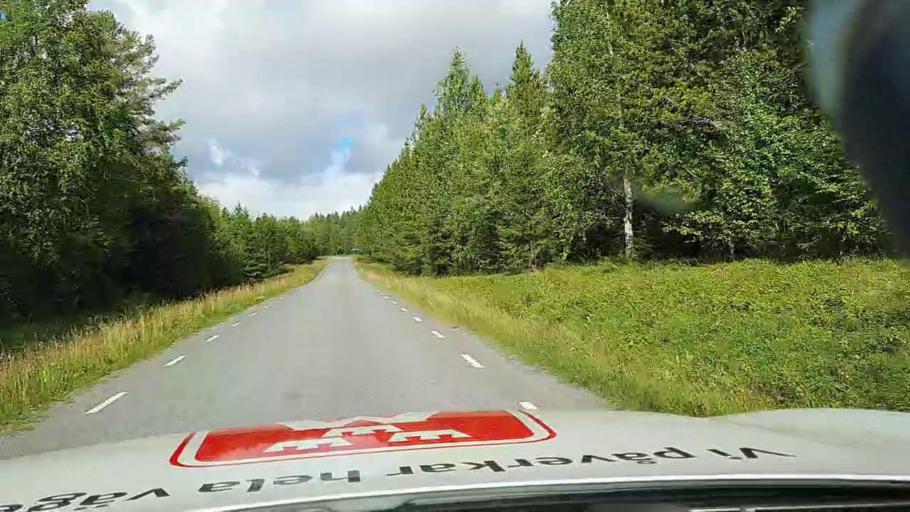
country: SE
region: Jaemtland
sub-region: Stroemsunds Kommun
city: Stroemsund
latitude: 63.7706
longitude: 15.2349
